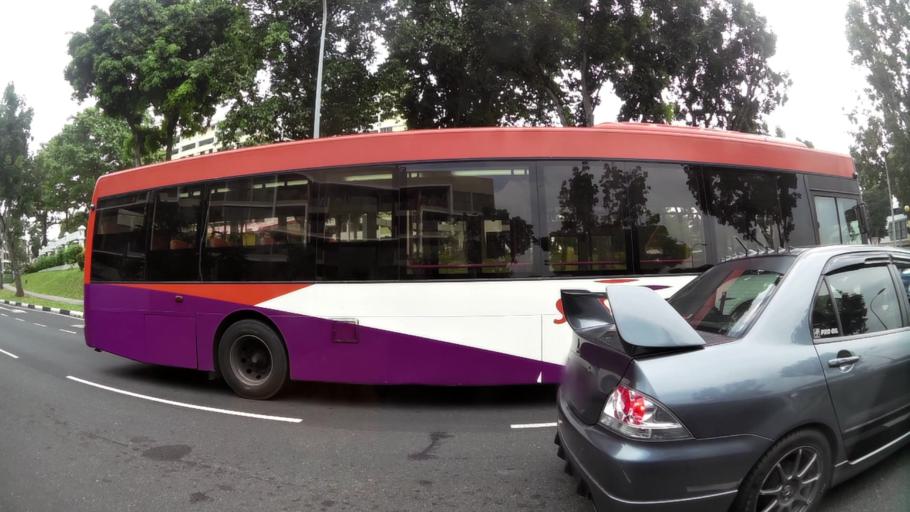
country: SG
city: Singapore
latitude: 1.3383
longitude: 103.9182
